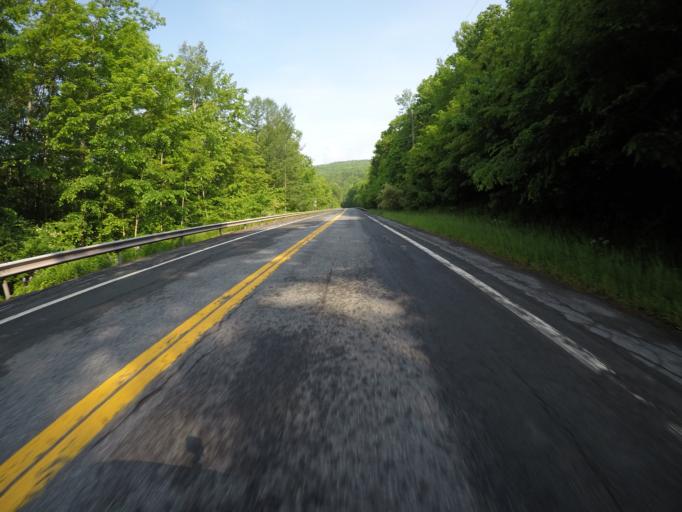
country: US
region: New York
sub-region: Sullivan County
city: Livingston Manor
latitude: 42.1252
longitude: -74.7059
